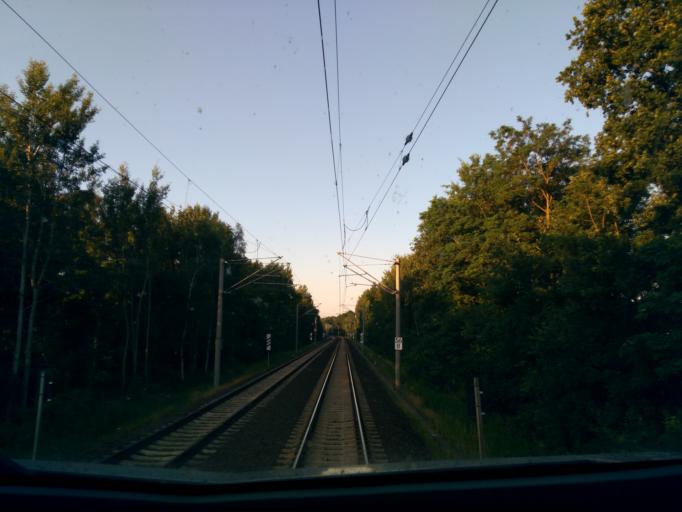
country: DE
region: Brandenburg
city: Halbe
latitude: 52.0560
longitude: 13.7220
